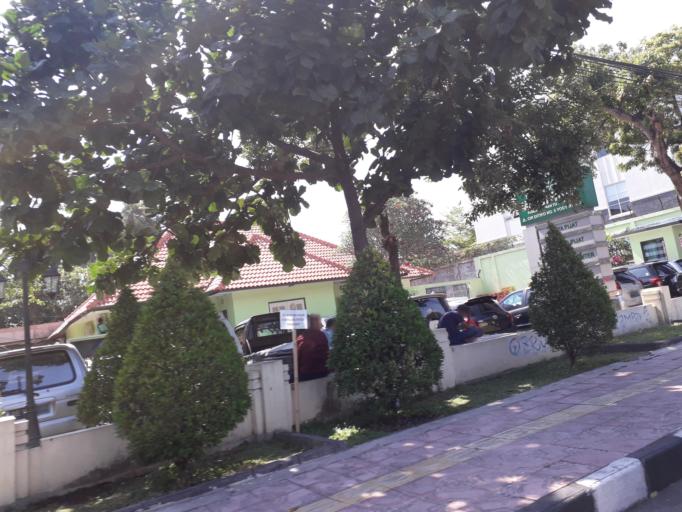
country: ID
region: Daerah Istimewa Yogyakarta
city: Yogyakarta
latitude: -7.7805
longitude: 110.3754
